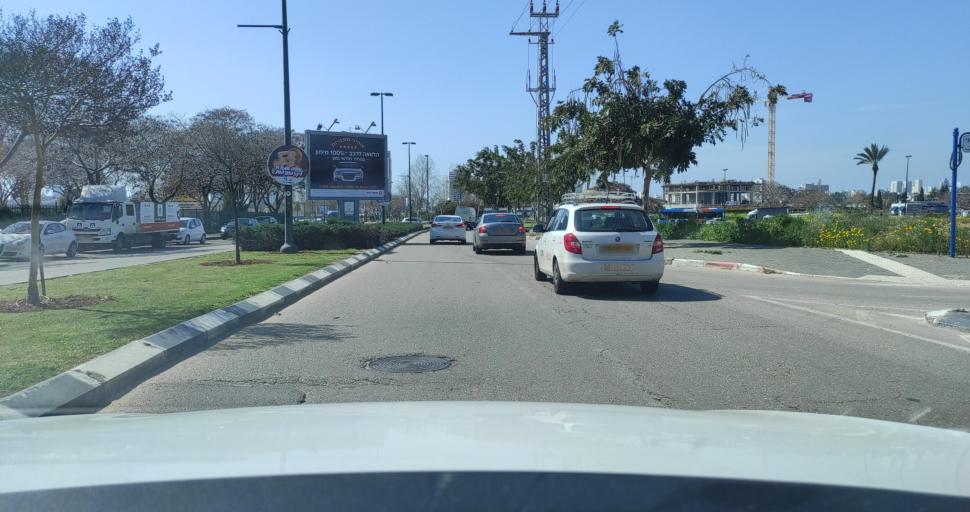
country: IL
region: Central District
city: Bet Yizhaq
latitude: 32.3118
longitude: 34.8739
